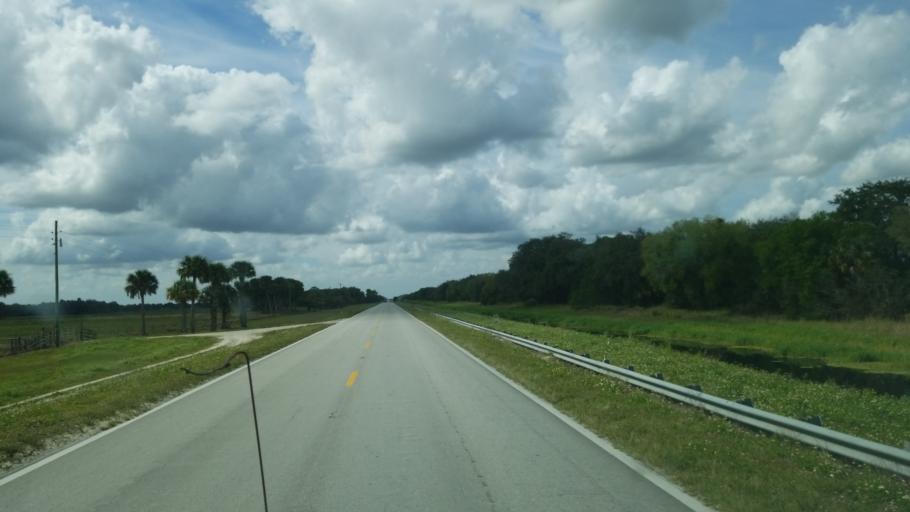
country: US
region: Florida
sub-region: Saint Lucie County
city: Lakewood Park
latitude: 27.4482
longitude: -80.5979
